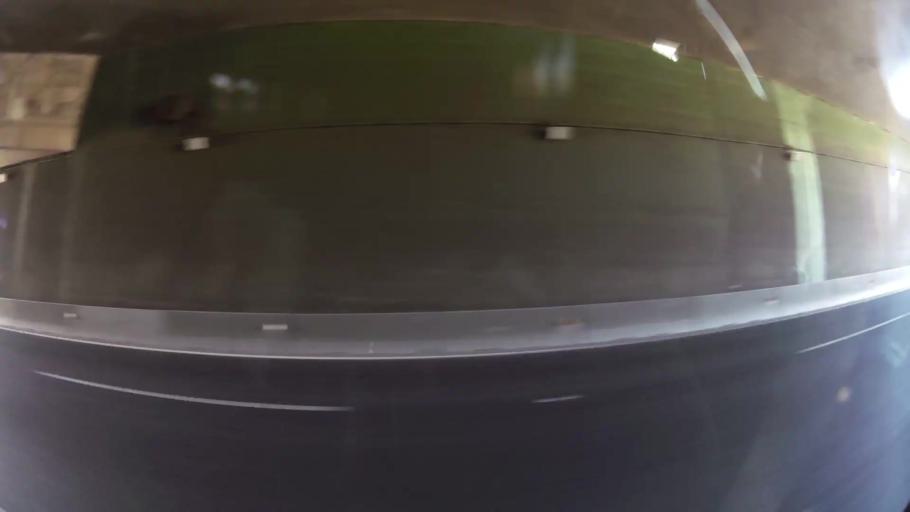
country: CL
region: Santiago Metropolitan
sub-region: Provincia de Santiago
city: Santiago
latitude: -33.4289
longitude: -70.6628
